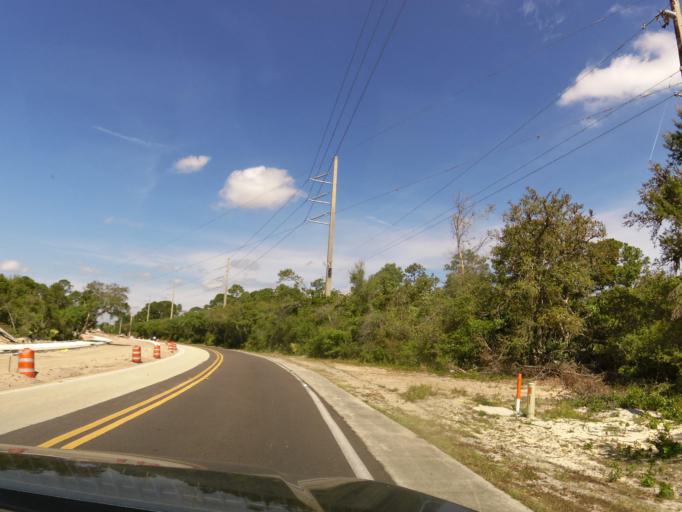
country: US
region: Florida
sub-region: Volusia County
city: Lake Helen
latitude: 28.9344
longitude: -81.2042
